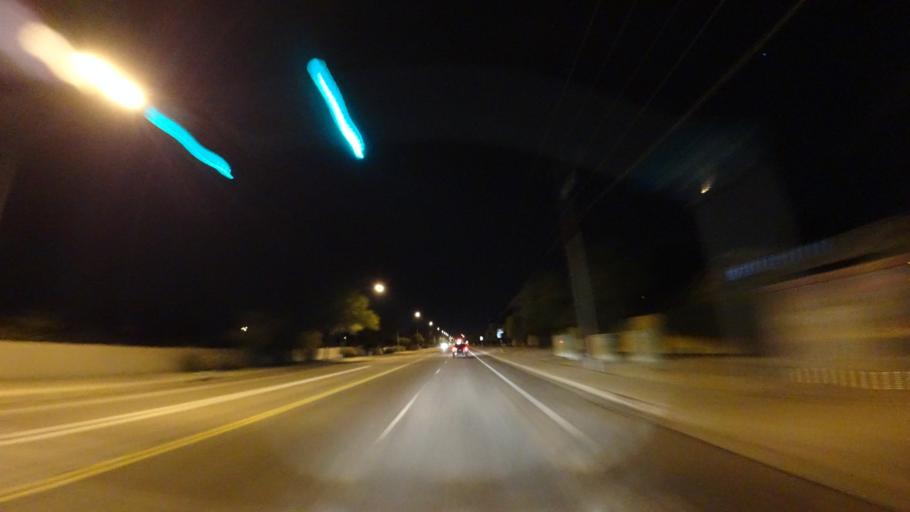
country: US
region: Arizona
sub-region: Maricopa County
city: Gilbert
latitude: 33.3936
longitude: -111.7612
